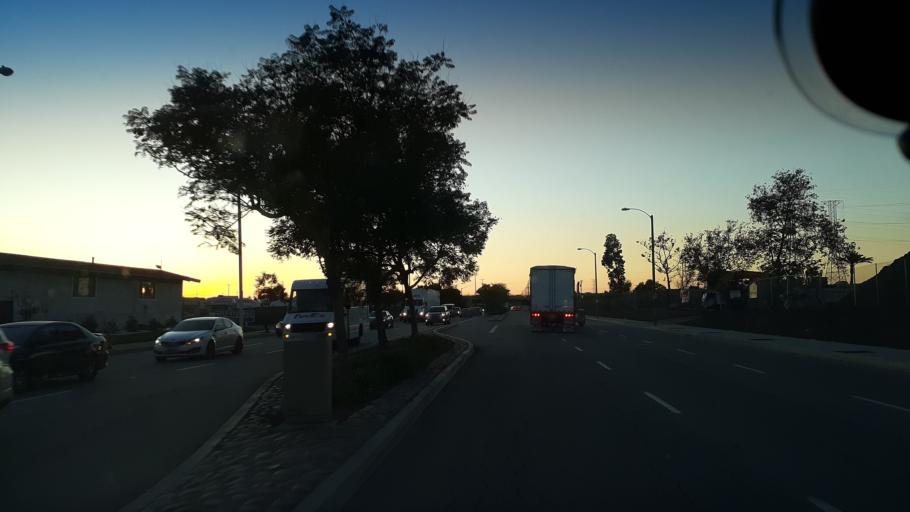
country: US
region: California
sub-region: Los Angeles County
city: Carson
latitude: 33.8463
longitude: -118.2810
